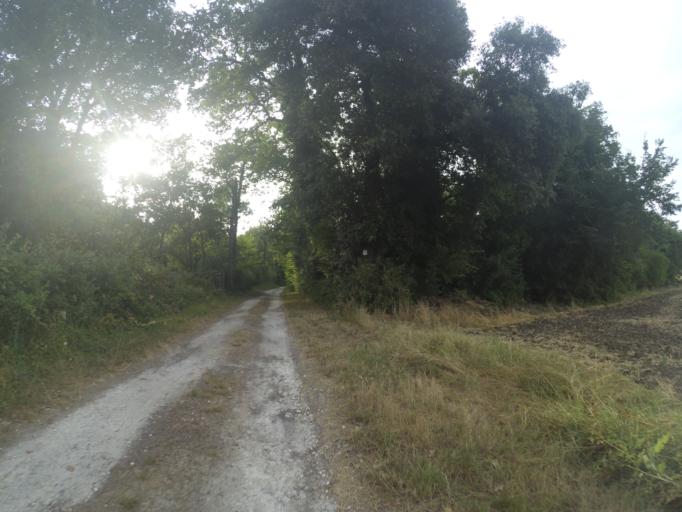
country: FR
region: Poitou-Charentes
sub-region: Departement de la Charente-Maritime
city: Meschers-sur-Gironde
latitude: 45.5769
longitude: -0.9737
